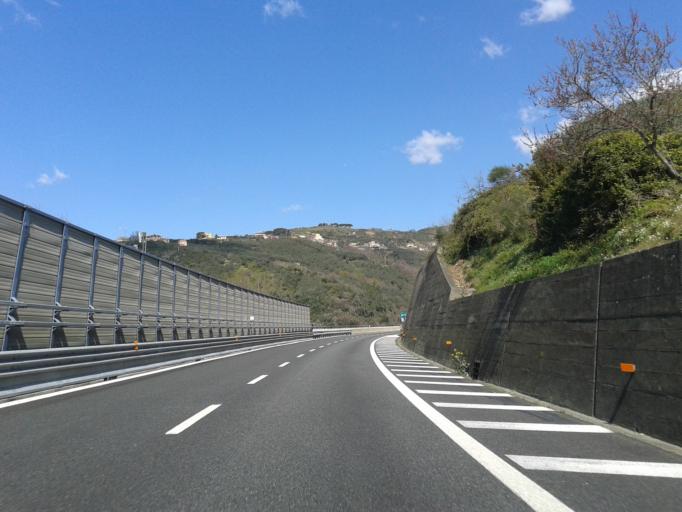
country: IT
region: Liguria
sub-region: Provincia di Genova
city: Sestri Levante
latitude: 44.2937
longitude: 9.3848
